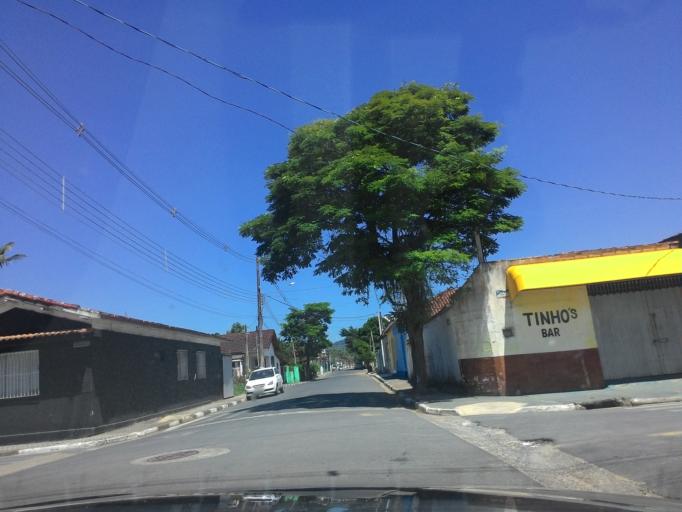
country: BR
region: Sao Paulo
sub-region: Pariquera-Acu
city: Pariquera Acu
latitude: -24.7145
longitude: -47.8843
